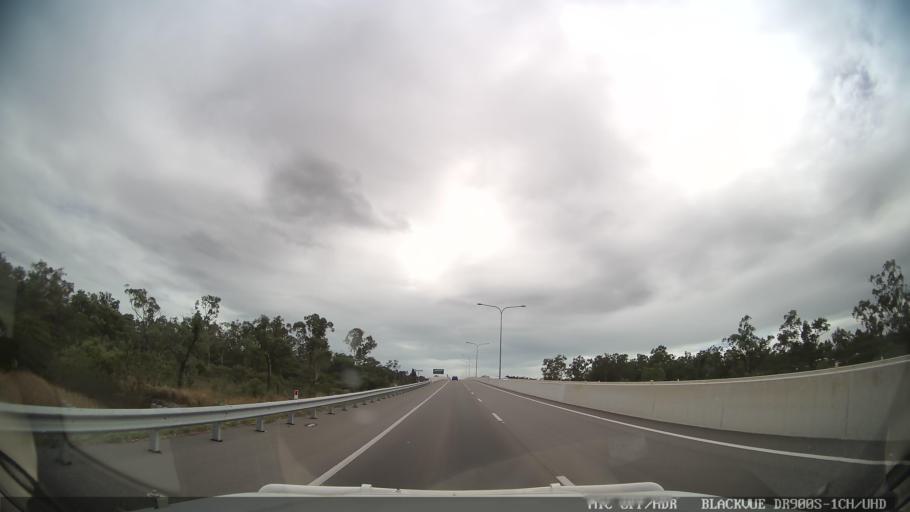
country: AU
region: Queensland
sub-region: Townsville
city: Bohle Plains
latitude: -19.2509
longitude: 146.6639
